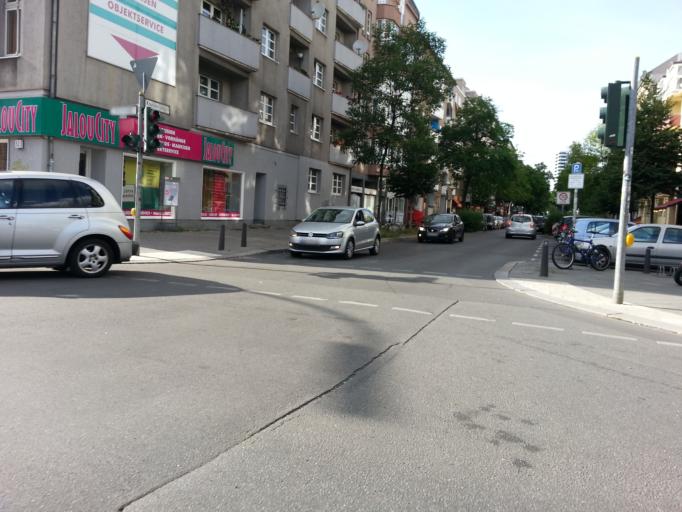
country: DE
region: Berlin
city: Halensee
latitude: 52.5067
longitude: 13.3094
